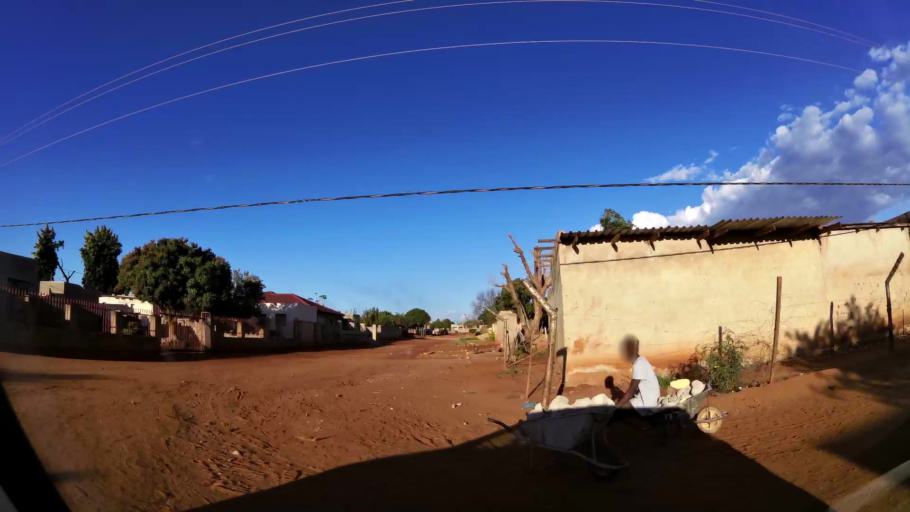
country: ZA
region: Limpopo
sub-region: Waterberg District Municipality
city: Mokopane
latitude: -24.1519
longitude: 28.9917
